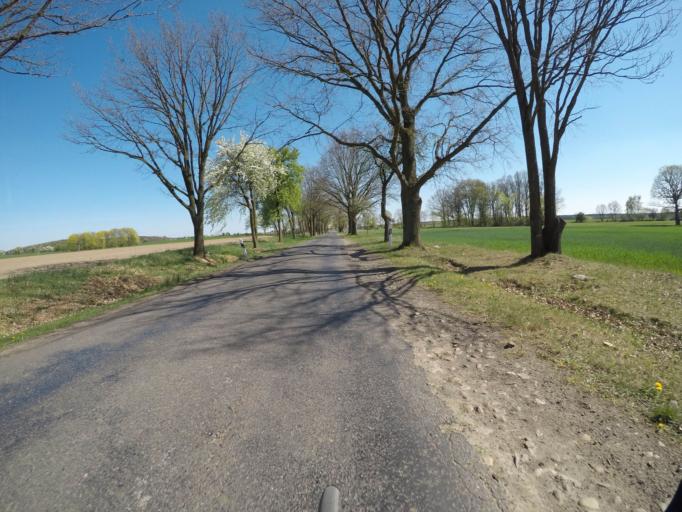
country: DE
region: Brandenburg
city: Strausberg
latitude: 52.6150
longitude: 13.8535
